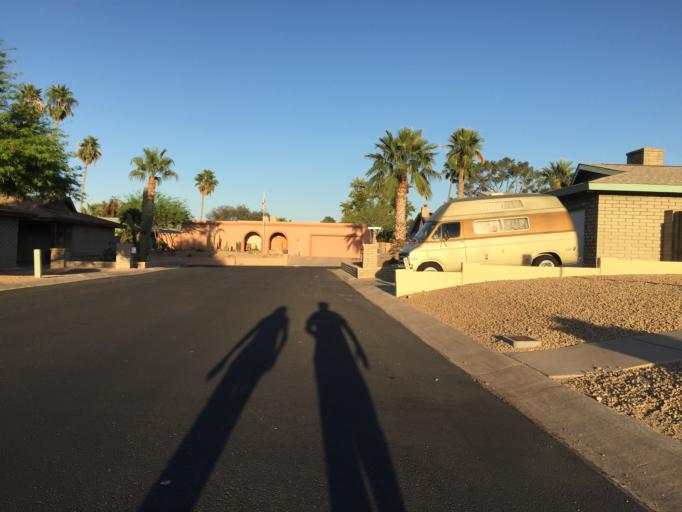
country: US
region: Arizona
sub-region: Maricopa County
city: Paradise Valley
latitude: 33.5698
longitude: -112.0165
